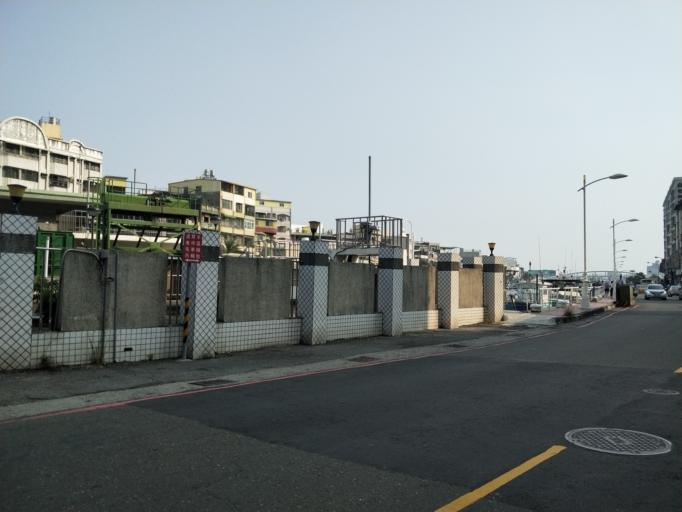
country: TW
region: Kaohsiung
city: Kaohsiung
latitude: 22.6241
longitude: 120.2694
